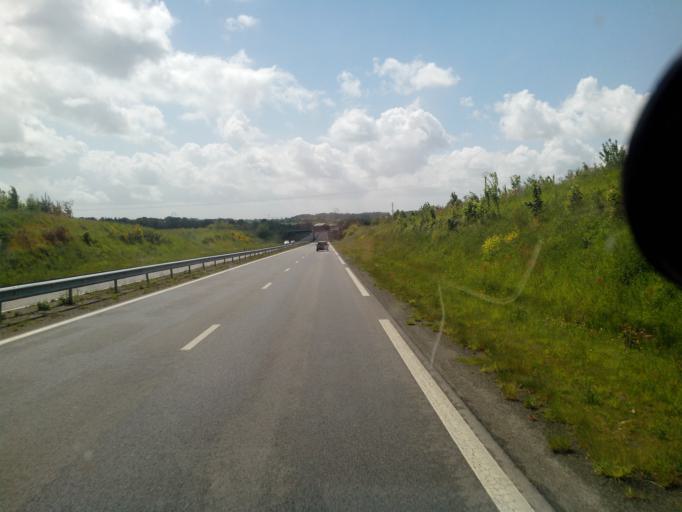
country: FR
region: Brittany
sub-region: Departement d'Ille-et-Vilaine
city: Betton
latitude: 48.1648
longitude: -1.6265
